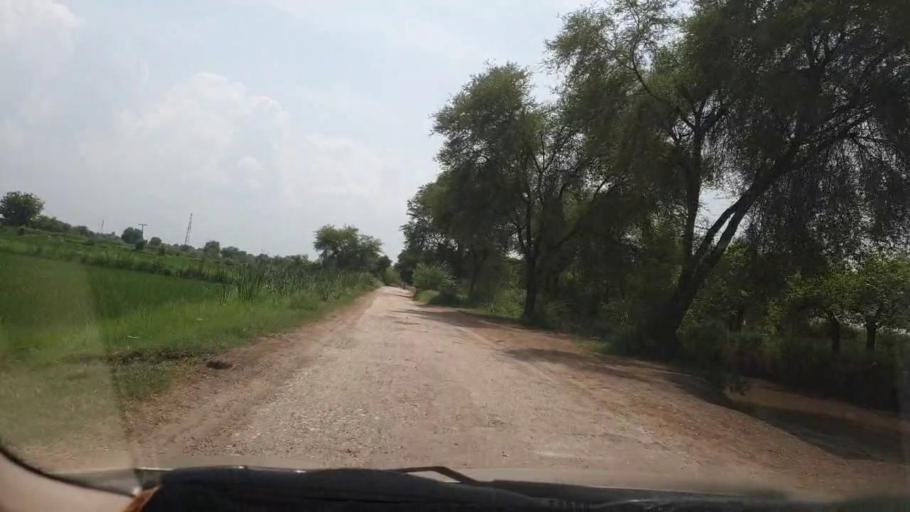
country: PK
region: Sindh
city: Larkana
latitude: 27.5882
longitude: 68.1191
